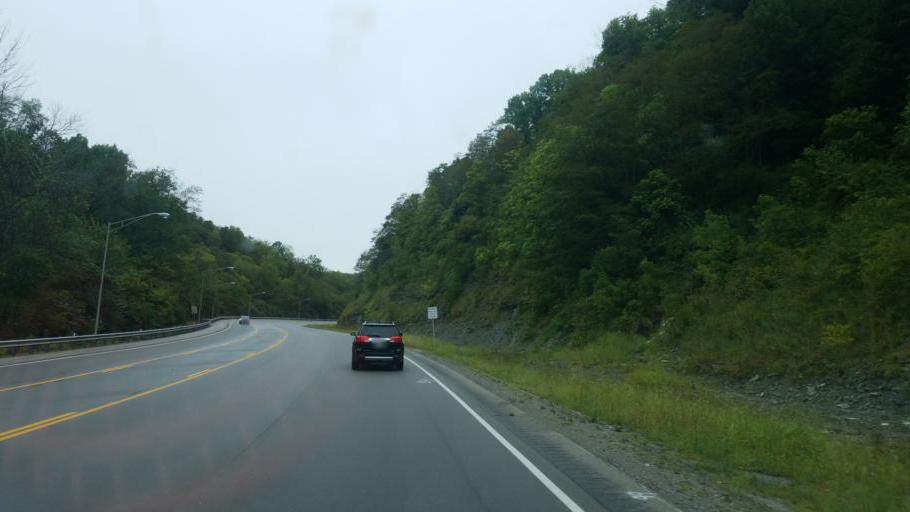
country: US
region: Ohio
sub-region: Brown County
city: Aberdeen
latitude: 38.6406
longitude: -83.7660
